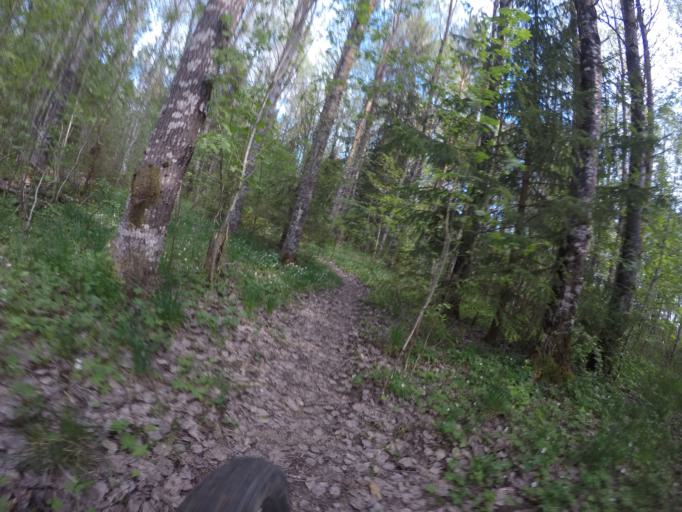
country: SE
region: Vaestmanland
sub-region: Vasteras
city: Vasteras
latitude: 59.6554
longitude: 16.5080
